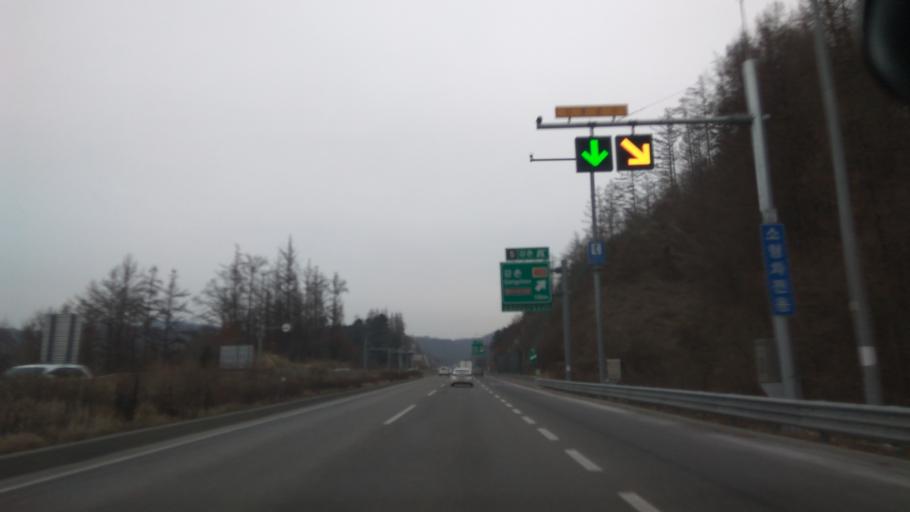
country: KR
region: Gangwon-do
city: Sindong
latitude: 37.7317
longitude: 127.6175
